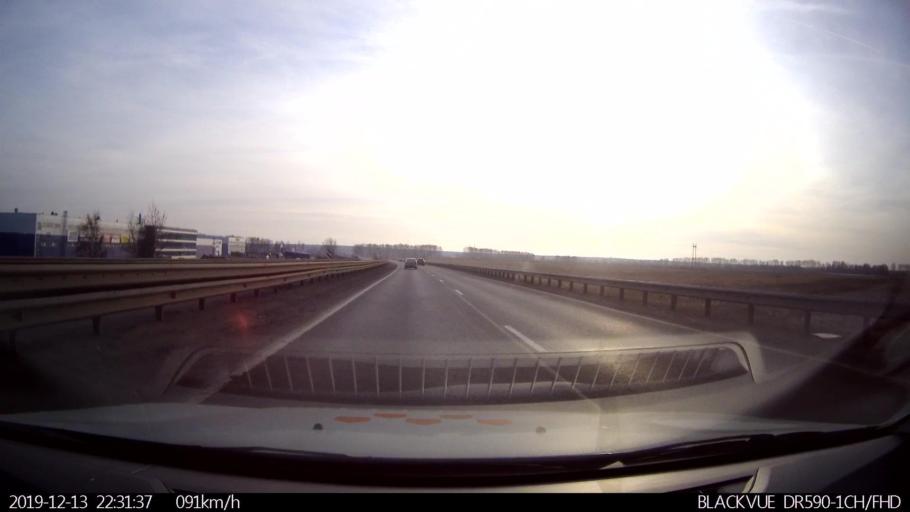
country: RU
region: Nizjnij Novgorod
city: Afonino
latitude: 56.2153
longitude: 44.0791
